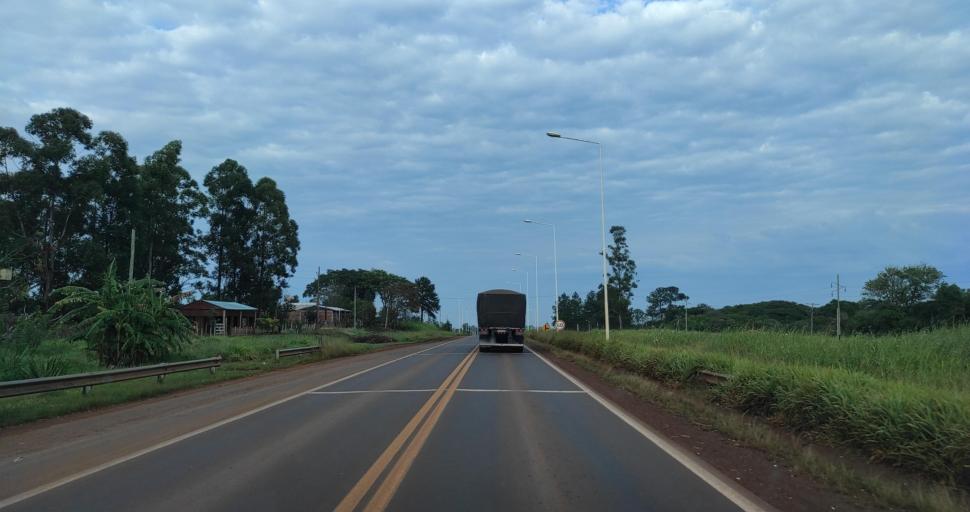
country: AR
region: Corrientes
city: Gobernador Ingeniero Valentin Virasoro
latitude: -27.9647
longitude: -56.0063
